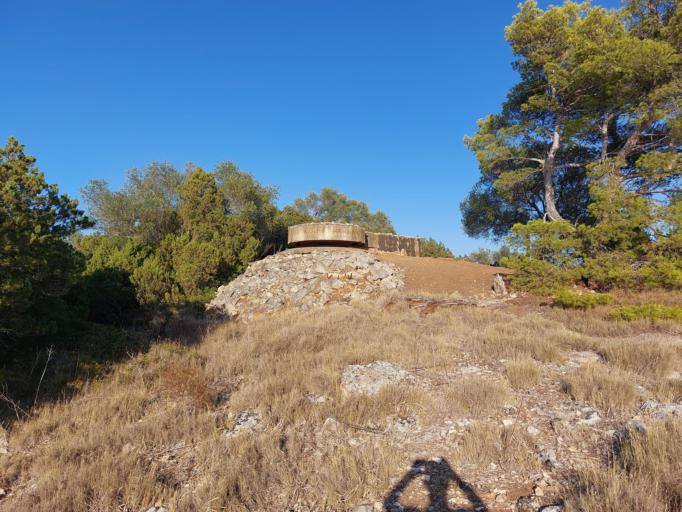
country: HR
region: Dubrovacko-Neretvanska
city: Smokvica
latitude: 42.7744
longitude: 16.7858
